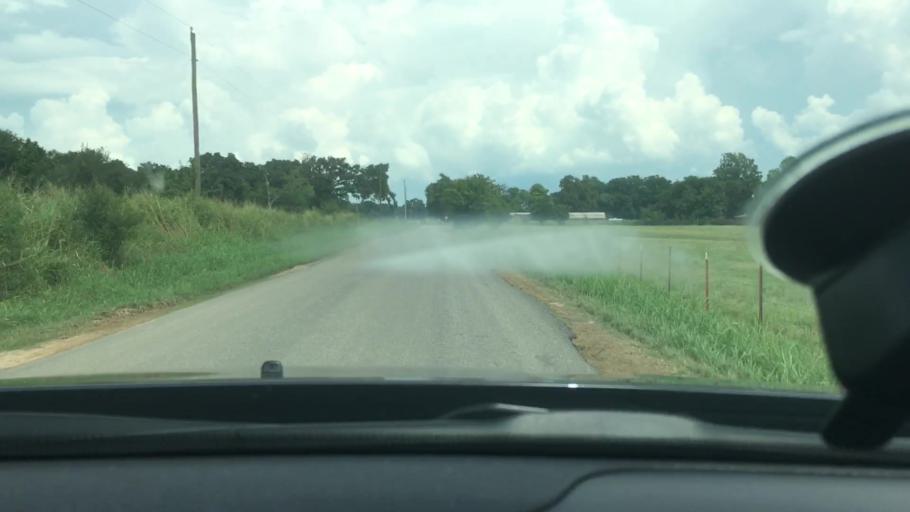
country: US
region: Oklahoma
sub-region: Carter County
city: Dickson
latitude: 34.1995
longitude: -96.8982
